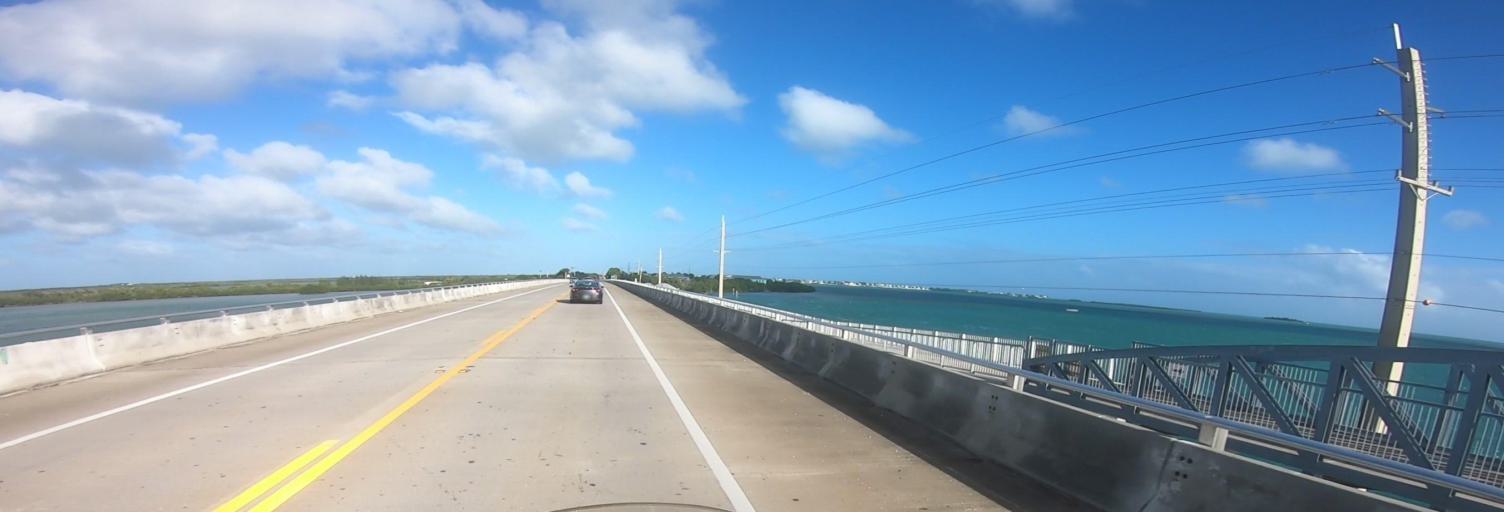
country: US
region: Florida
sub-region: Monroe County
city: Cudjoe Key
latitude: 24.6626
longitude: -81.4666
